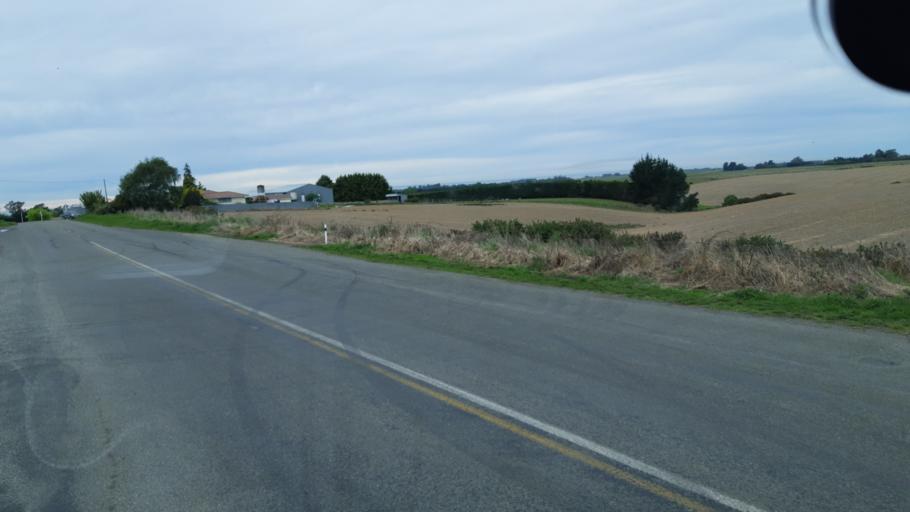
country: NZ
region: Canterbury
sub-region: Timaru District
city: Timaru
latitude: -44.4101
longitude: 171.1712
